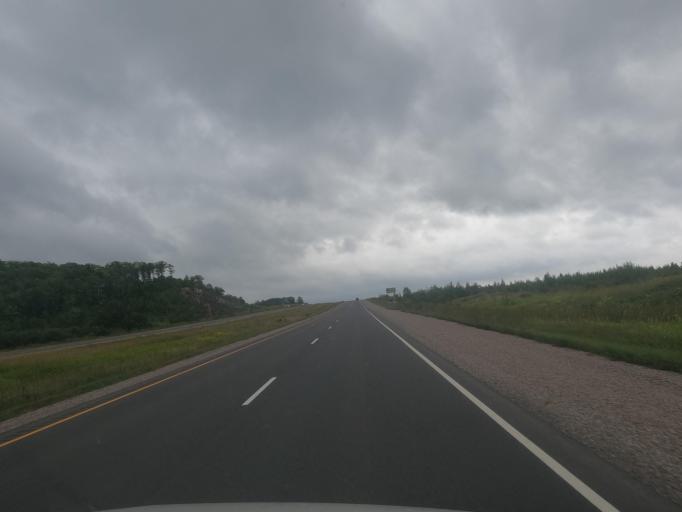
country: CA
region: Ontario
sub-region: Algoma
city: Sault Ste. Marie
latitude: 46.4641
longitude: -84.0592
